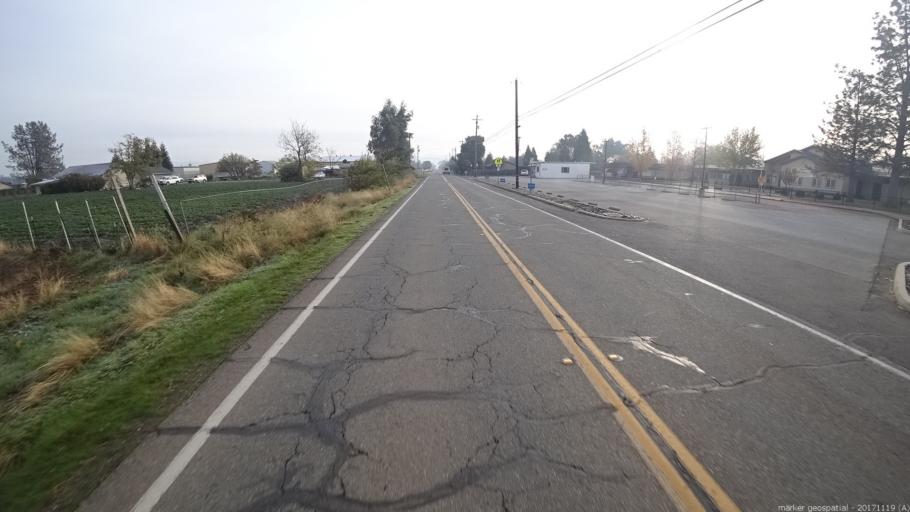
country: US
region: California
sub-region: Shasta County
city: Anderson
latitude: 40.4804
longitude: -122.2755
